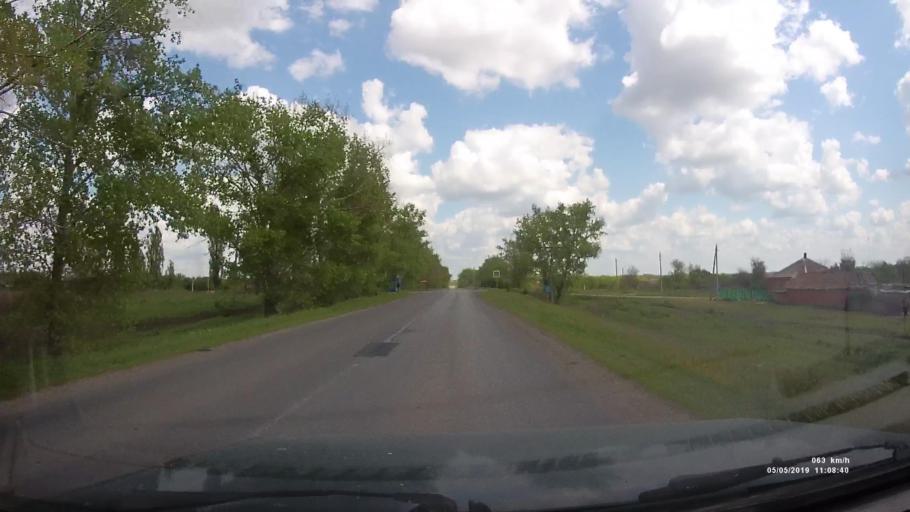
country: RU
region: Rostov
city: Ust'-Donetskiy
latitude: 47.7355
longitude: 40.9165
